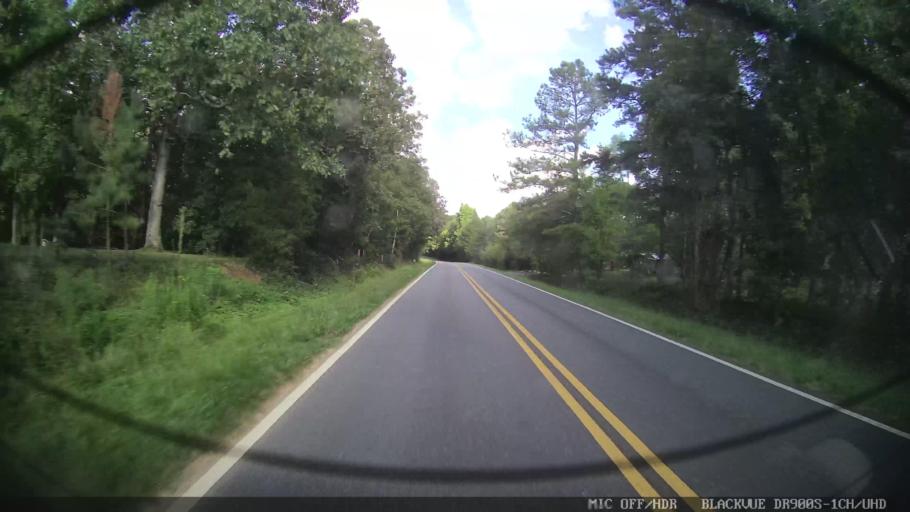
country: US
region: Georgia
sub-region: Bartow County
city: Euharlee
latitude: 34.1780
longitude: -85.0100
